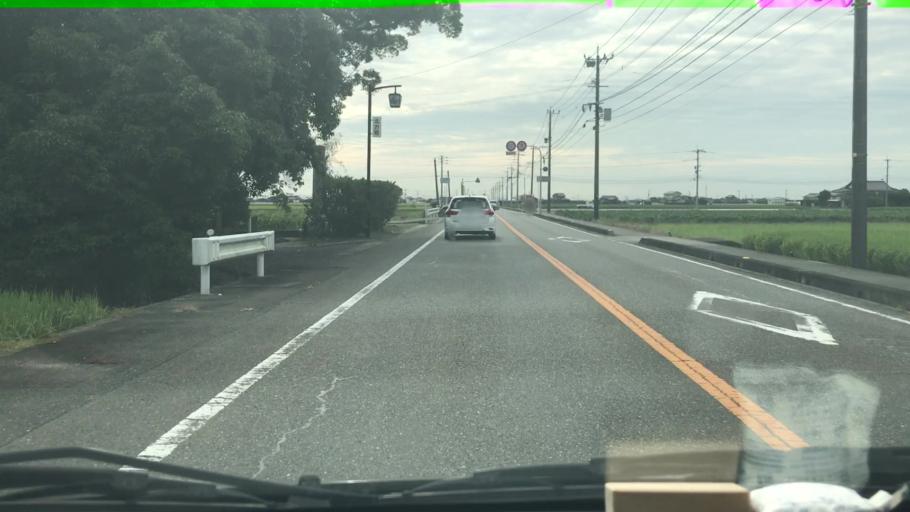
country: JP
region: Saga Prefecture
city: Takeocho-takeo
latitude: 33.2034
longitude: 130.0939
